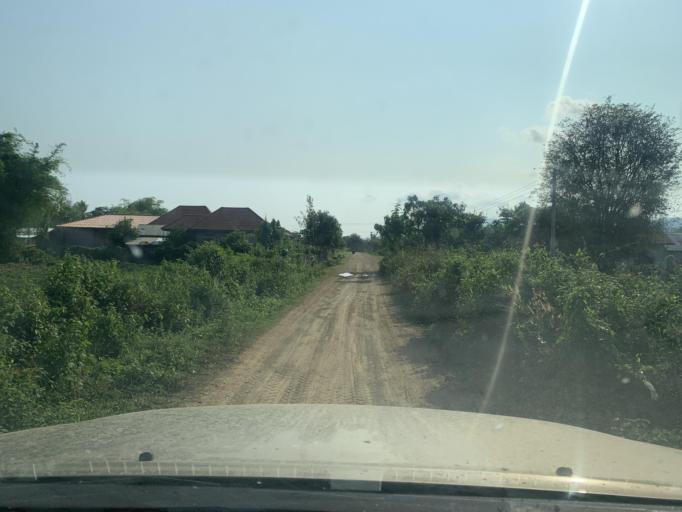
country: TH
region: Uttaradit
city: Ban Khok
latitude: 18.2829
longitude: 101.3159
